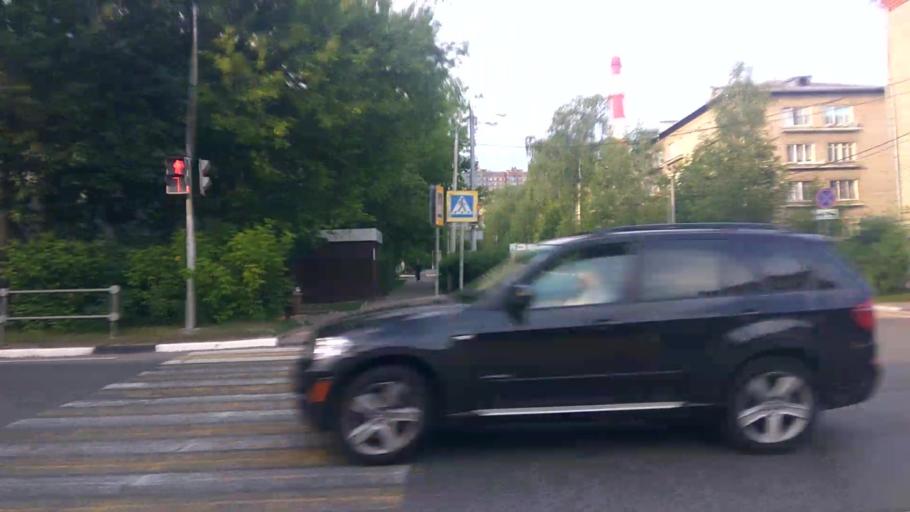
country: RU
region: Moskovskaya
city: Mytishchi
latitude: 55.9127
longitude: 37.7323
